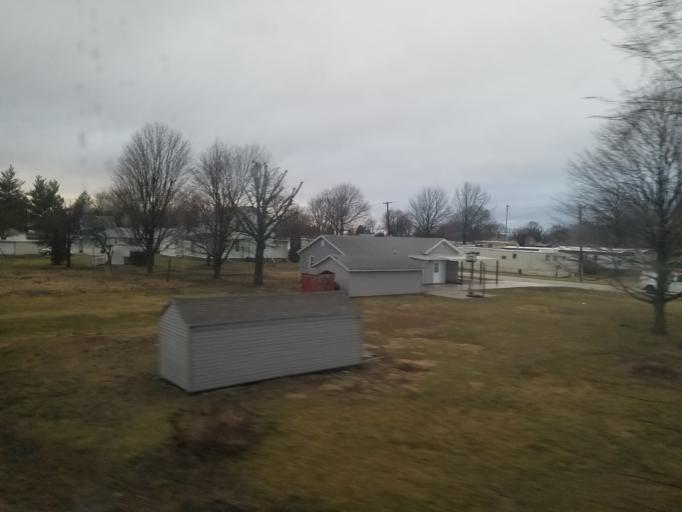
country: US
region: Illinois
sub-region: Warren County
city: Monmouth
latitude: 40.9056
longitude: -90.6559
